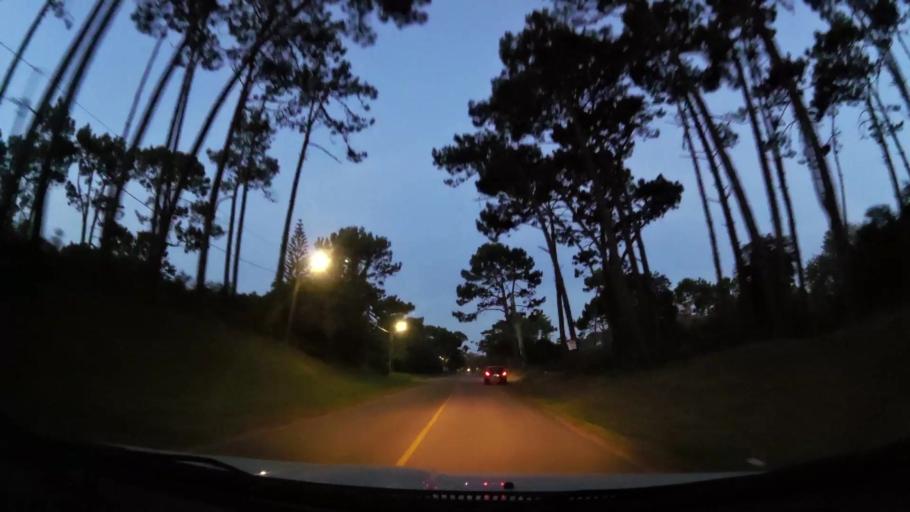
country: UY
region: Maldonado
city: Punta del Este
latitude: -34.9429
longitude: -54.9256
